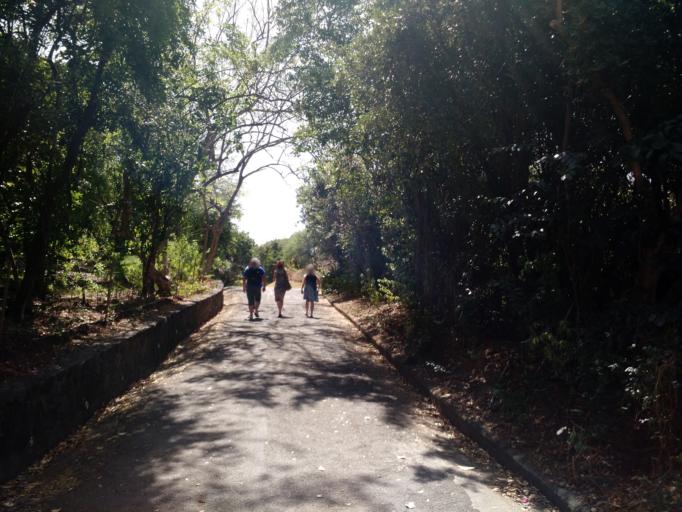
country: VC
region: Grenadines
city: Port Elizabeth
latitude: 12.8858
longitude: -61.1807
